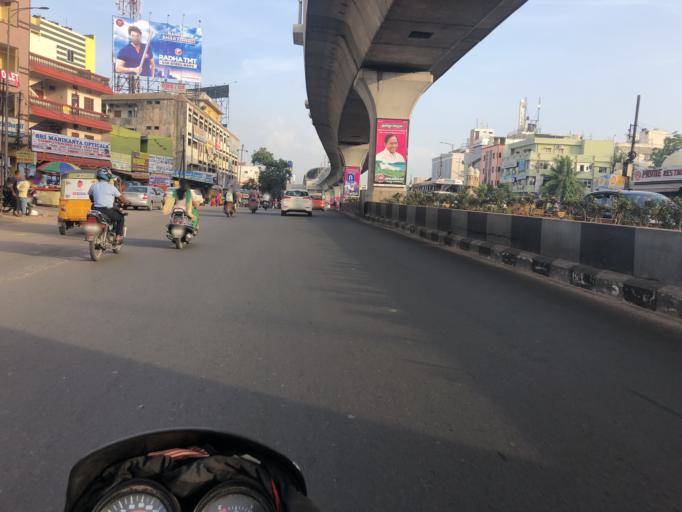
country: IN
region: Telangana
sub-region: Rangareddi
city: Kukatpalli
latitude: 17.4445
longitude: 78.4401
